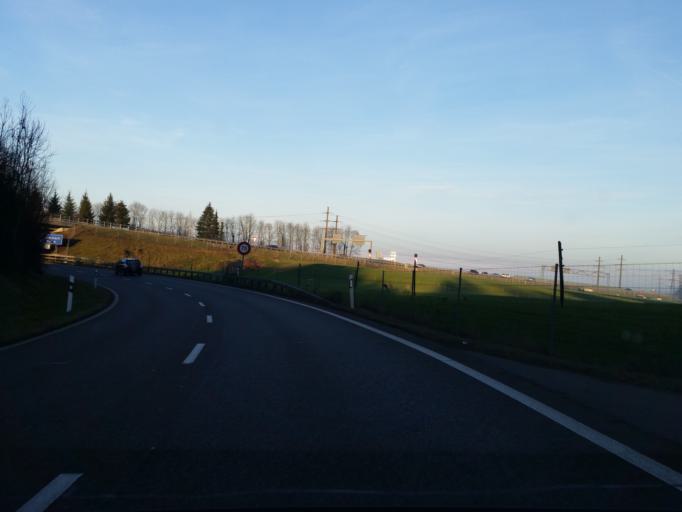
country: CH
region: Saint Gallen
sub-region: Wahlkreis Rorschach
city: Morschwil
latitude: 47.4684
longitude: 9.4454
